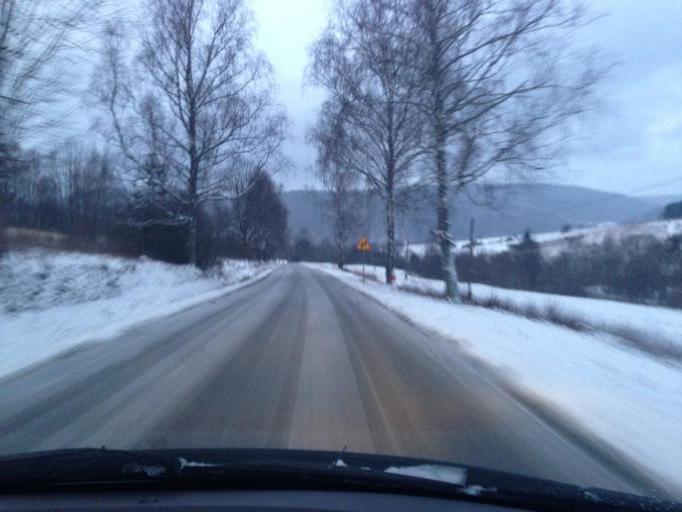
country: PL
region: Subcarpathian Voivodeship
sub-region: Powiat jasielski
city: Krempna
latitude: 49.5220
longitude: 21.5021
